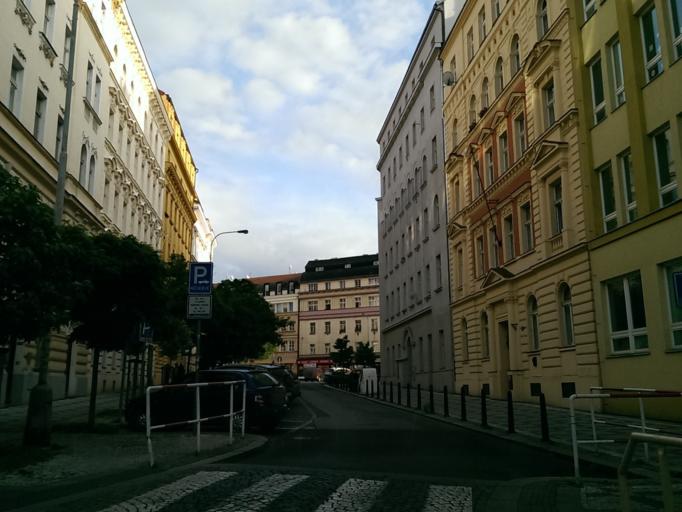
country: CZ
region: Praha
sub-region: Praha 8
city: Karlin
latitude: 50.0743
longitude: 14.4406
